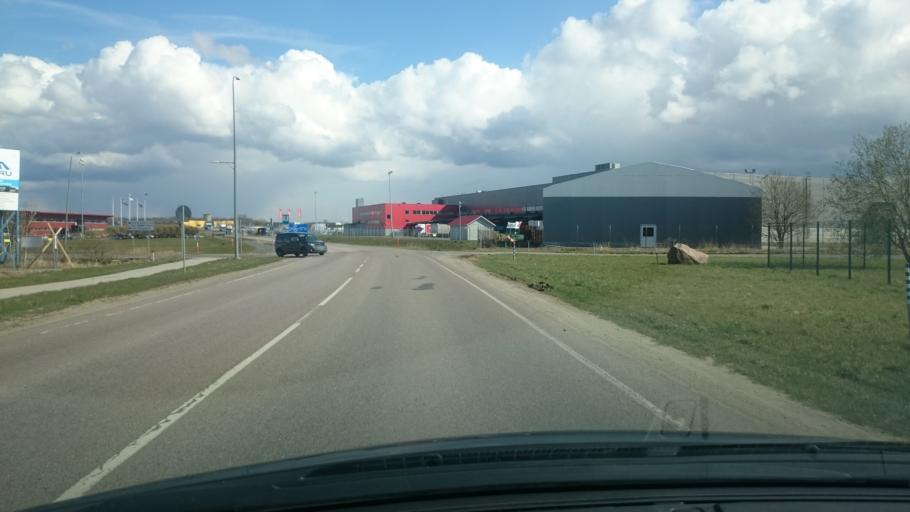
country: EE
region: Harju
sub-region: Rae vald
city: Jueri
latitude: 59.3606
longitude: 24.8827
